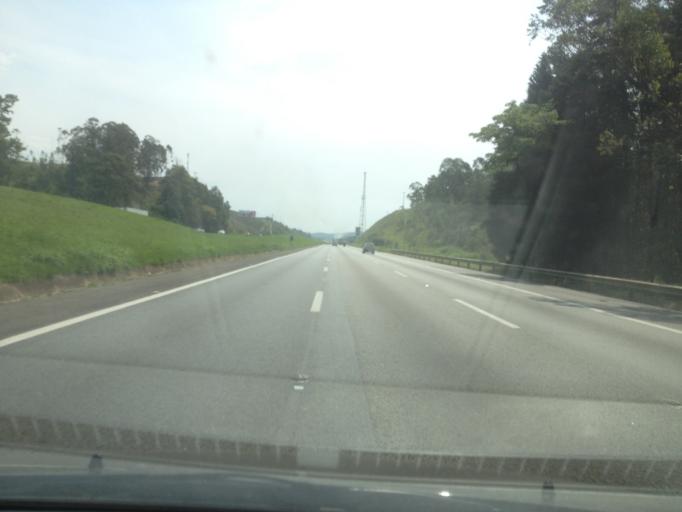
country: BR
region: Sao Paulo
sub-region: Sao Roque
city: Sao Roque
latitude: -23.4214
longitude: -47.1713
